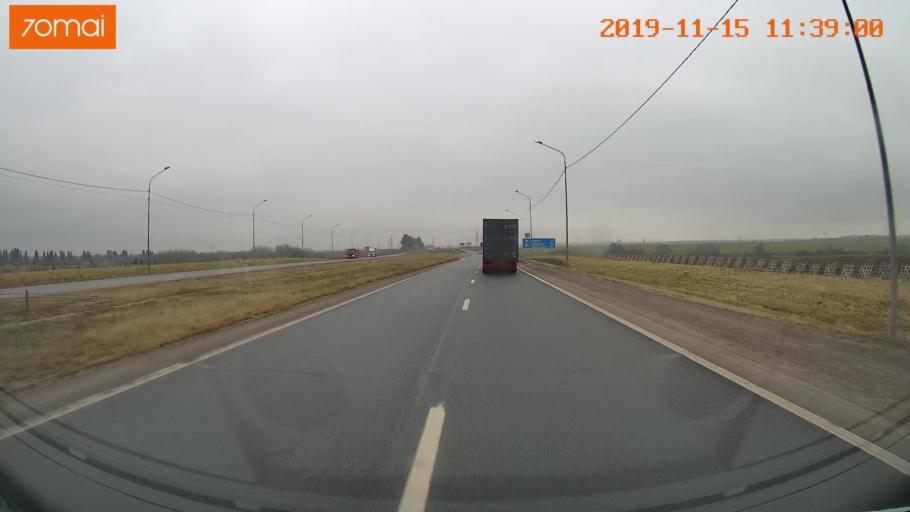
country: RU
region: Vologda
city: Molochnoye
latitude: 59.2109
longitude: 39.7118
